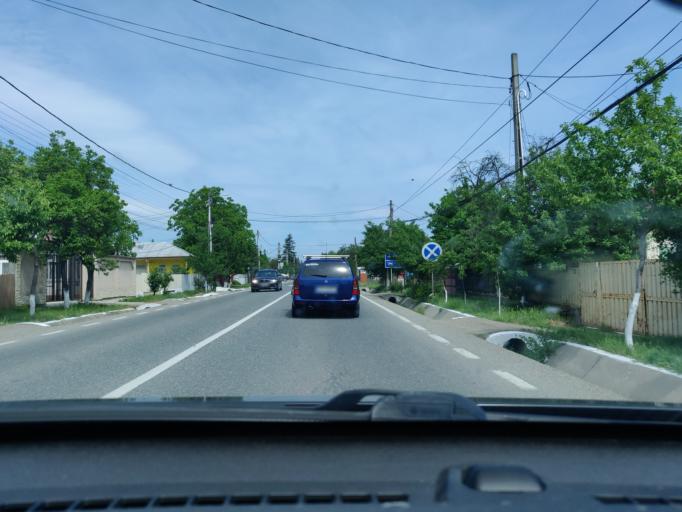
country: RO
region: Vrancea
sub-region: Comuna Bolotesti
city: Gagesti
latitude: 45.8528
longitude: 27.0573
